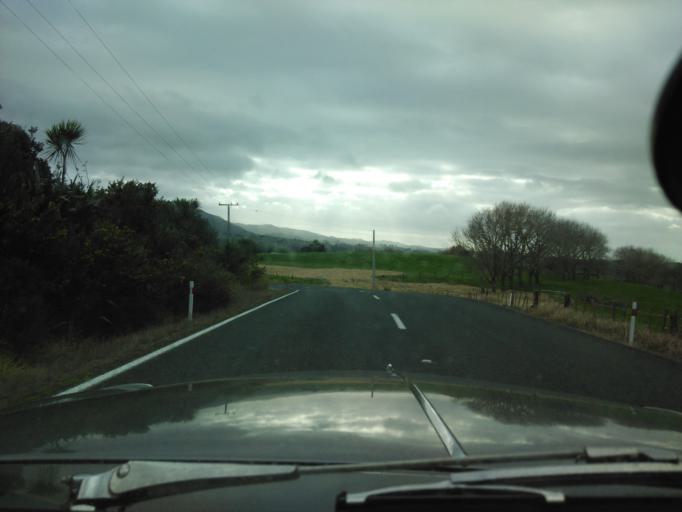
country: NZ
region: Auckland
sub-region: Auckland
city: Wellsford
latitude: -36.1750
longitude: 174.4163
